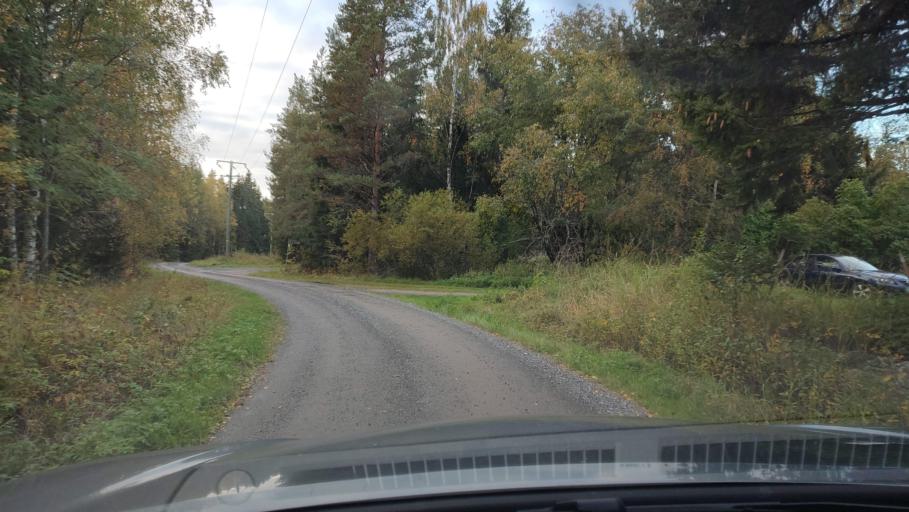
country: FI
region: Ostrobothnia
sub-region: Sydosterbotten
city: Kristinestad
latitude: 62.2316
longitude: 21.4045
